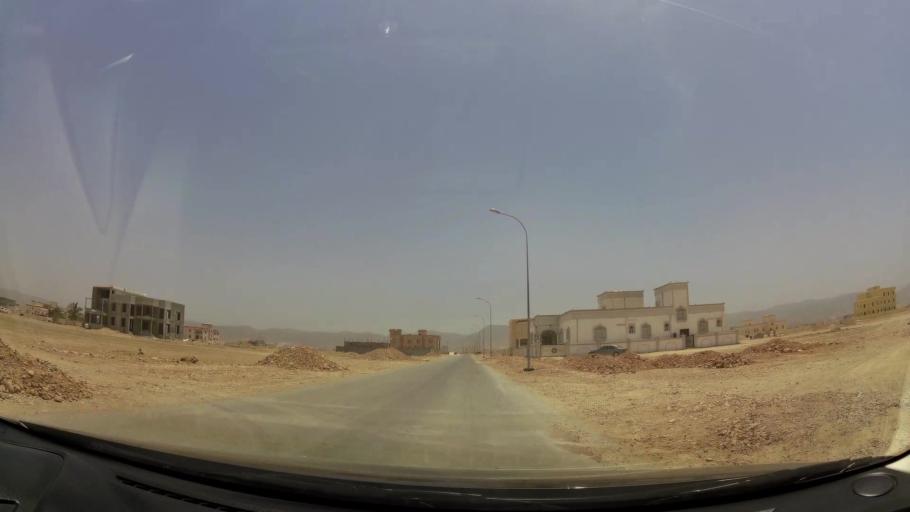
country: OM
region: Zufar
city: Salalah
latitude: 17.0947
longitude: 54.1838
